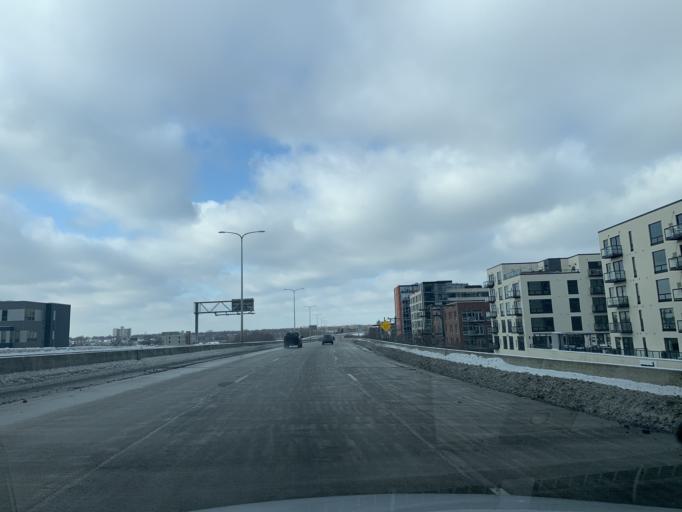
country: US
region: Minnesota
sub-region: Hennepin County
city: Minneapolis
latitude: 44.9849
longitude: -93.2780
